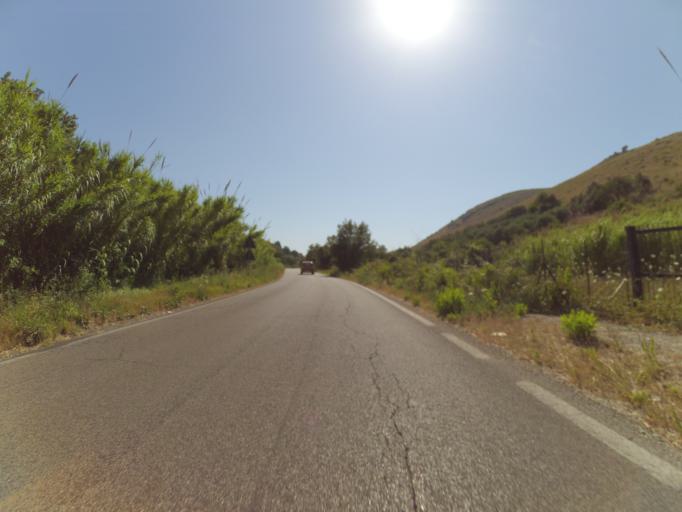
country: IT
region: Latium
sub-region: Provincia di Latina
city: Gaeta
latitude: 41.2330
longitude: 13.5179
